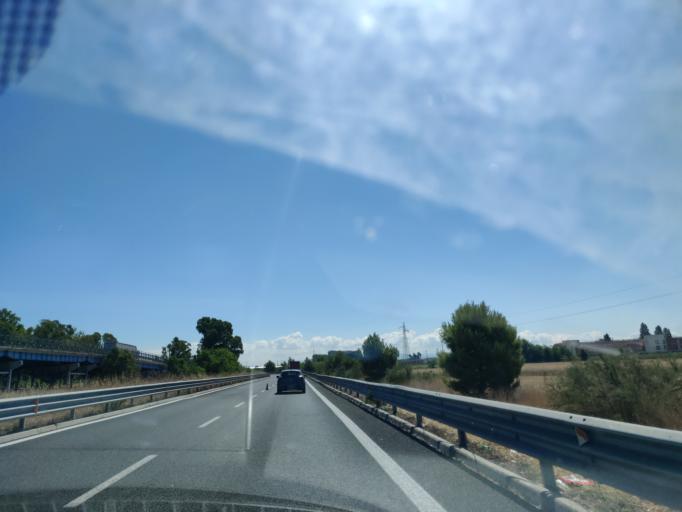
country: IT
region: Latium
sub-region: Citta metropolitana di Roma Capitale
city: Npp 23 (Parco Leonardo)
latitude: 41.8090
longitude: 12.3098
